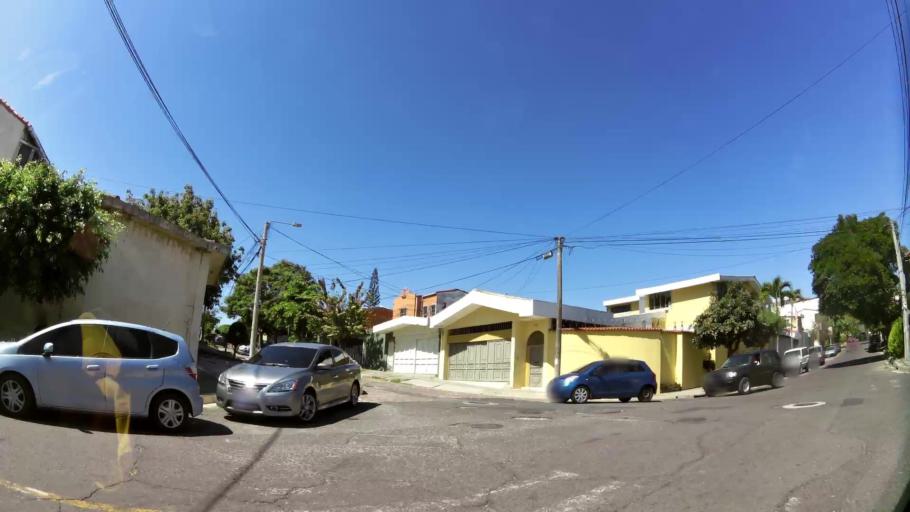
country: SV
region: La Libertad
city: Santa Tecla
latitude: 13.6683
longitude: -89.2792
